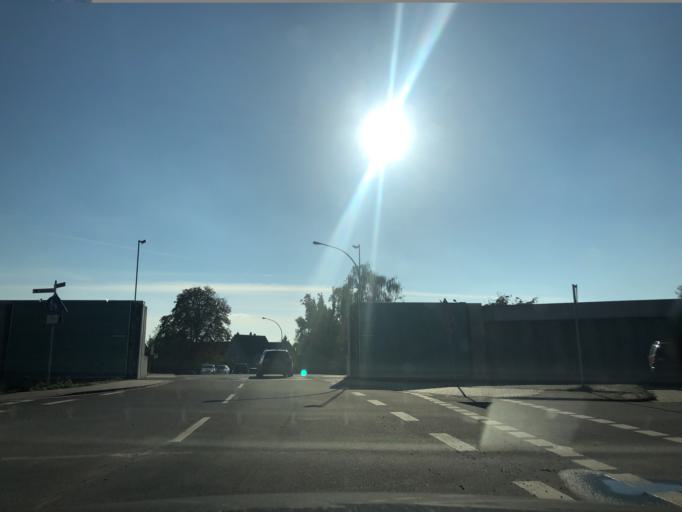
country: DE
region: Lower Saxony
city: Lemwerder
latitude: 53.1790
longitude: 8.5573
